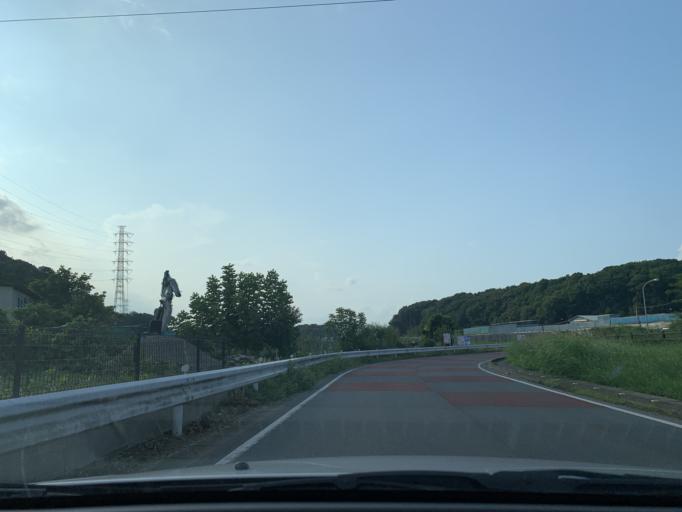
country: JP
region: Chiba
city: Nagareyama
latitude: 35.8568
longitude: 139.9320
